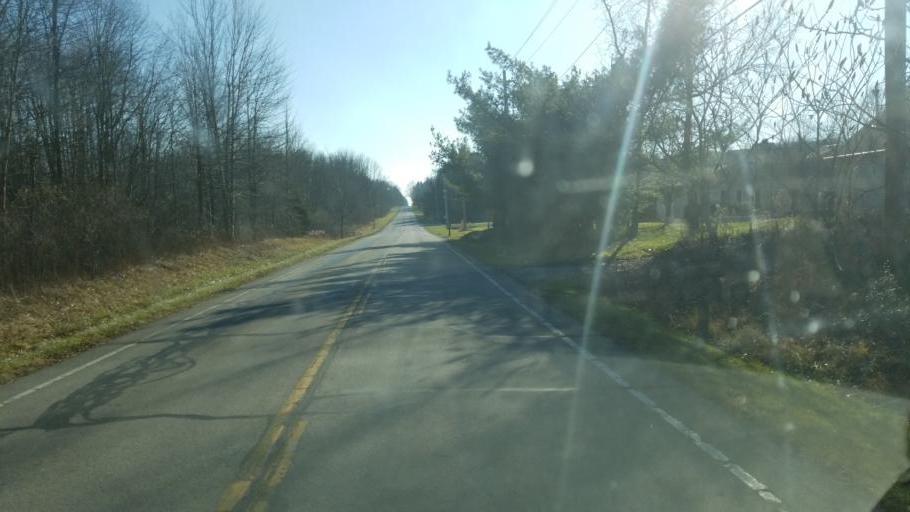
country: US
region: Ohio
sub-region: Geauga County
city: Bainbridge
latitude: 41.4006
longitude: -81.2464
